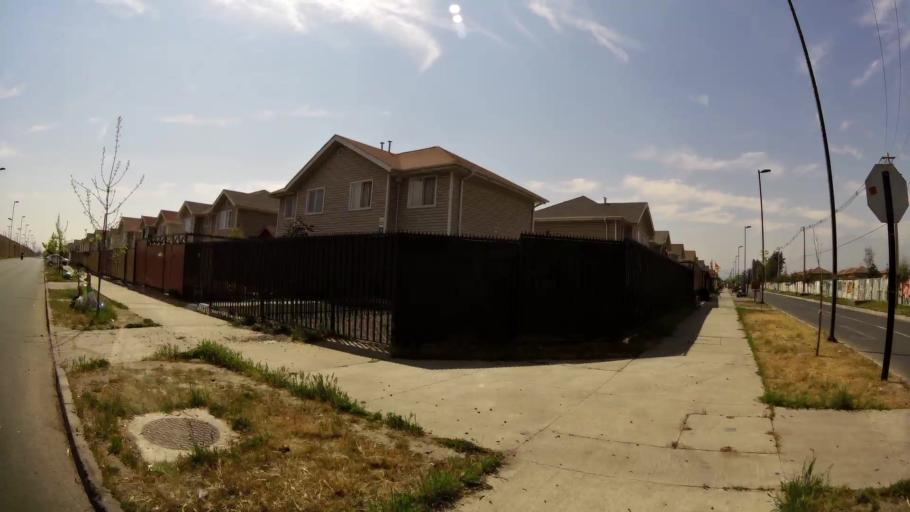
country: CL
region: Santiago Metropolitan
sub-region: Provincia de Cordillera
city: Puente Alto
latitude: -33.6002
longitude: -70.5942
